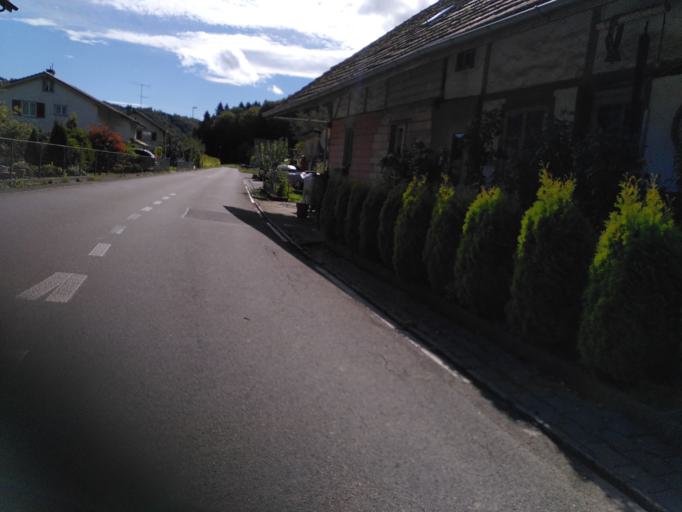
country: CH
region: Bern
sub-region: Oberaargau
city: Seeberg
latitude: 47.1380
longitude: 7.6721
